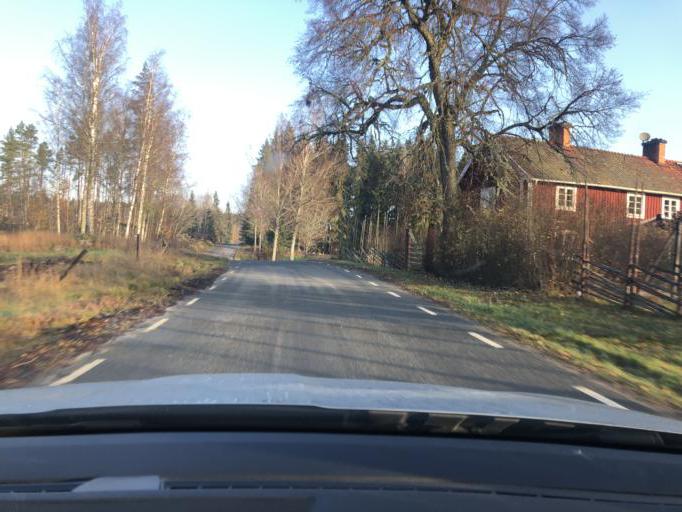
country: SE
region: Soedermanland
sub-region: Flens Kommun
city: Halleforsnas
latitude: 59.0881
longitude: 16.4278
